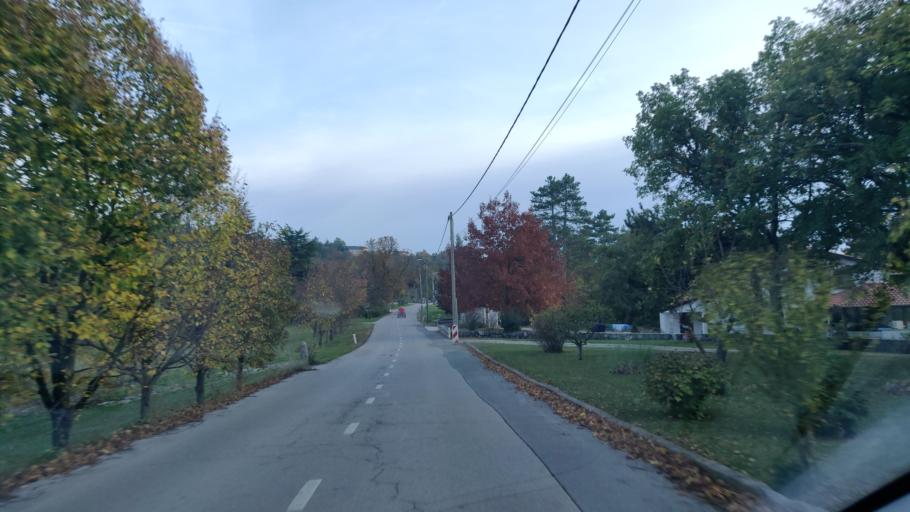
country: SI
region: Sezana
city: Sezana
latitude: 45.7856
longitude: 13.8659
